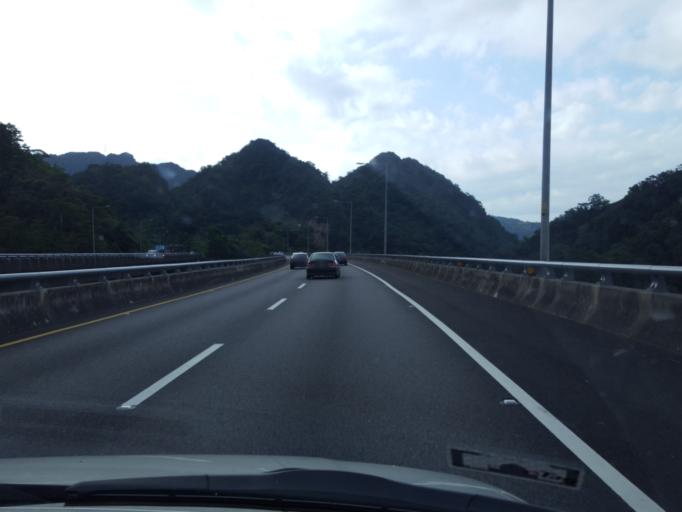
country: TW
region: Taipei
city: Taipei
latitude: 24.9813
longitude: 121.6725
